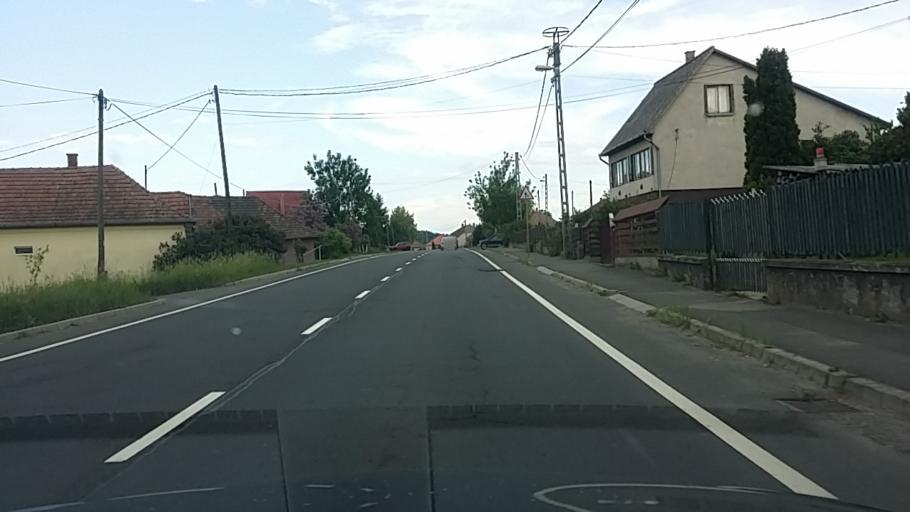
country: HU
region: Nograd
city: Nagyoroszi
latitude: 47.9745
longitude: 19.1194
